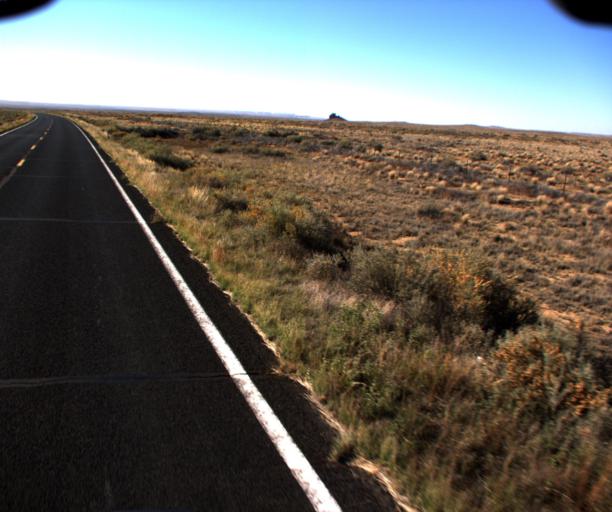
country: US
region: Arizona
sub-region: Navajo County
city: First Mesa
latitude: 35.7409
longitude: -110.5187
